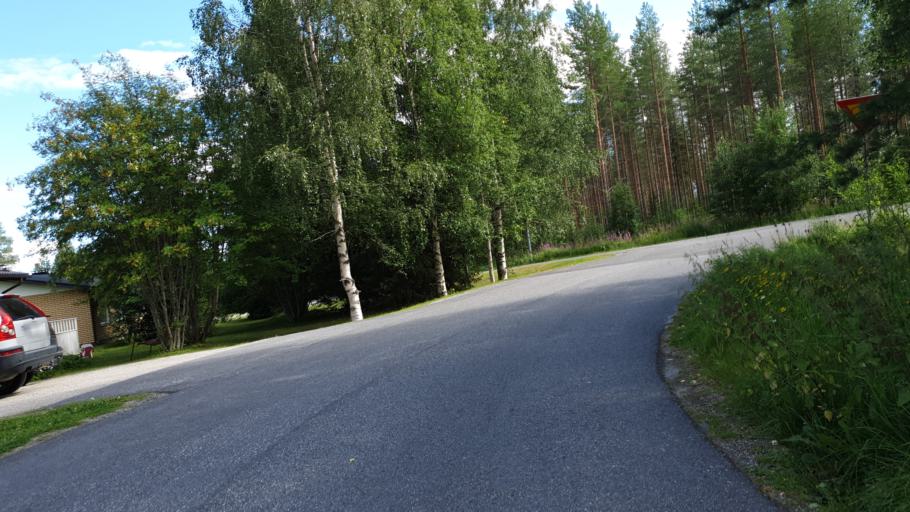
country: FI
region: Kainuu
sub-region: Kehys-Kainuu
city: Kuhmo
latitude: 64.1162
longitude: 29.5110
